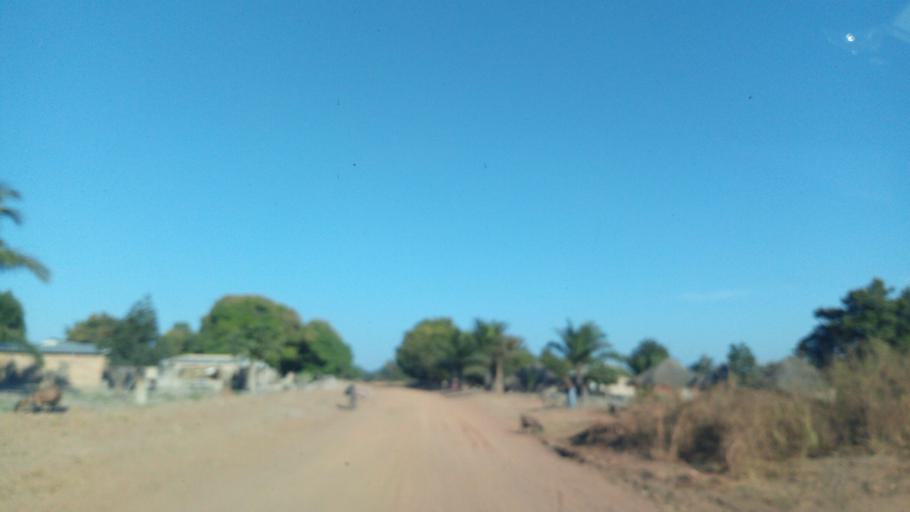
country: ZM
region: Luapula
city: Mwense
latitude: -10.4554
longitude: 28.5400
